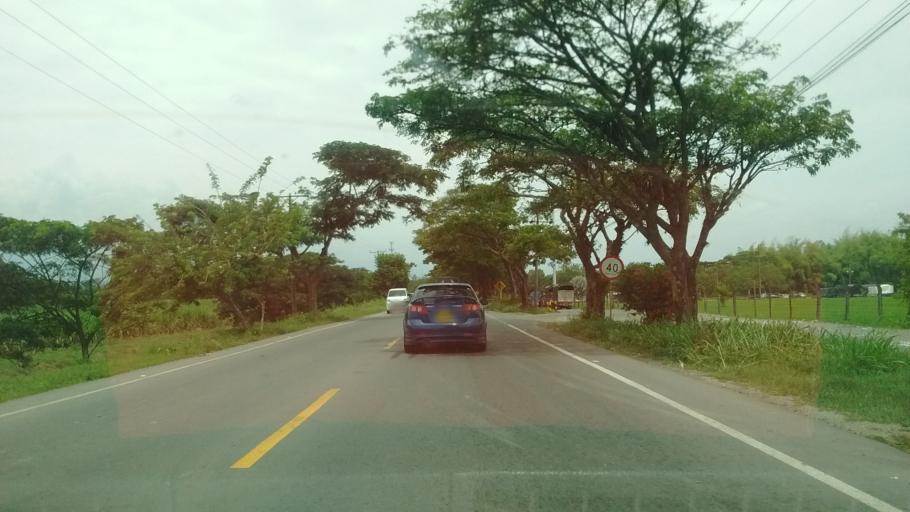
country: CO
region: Valle del Cauca
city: Jamundi
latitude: 3.2976
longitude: -76.4732
